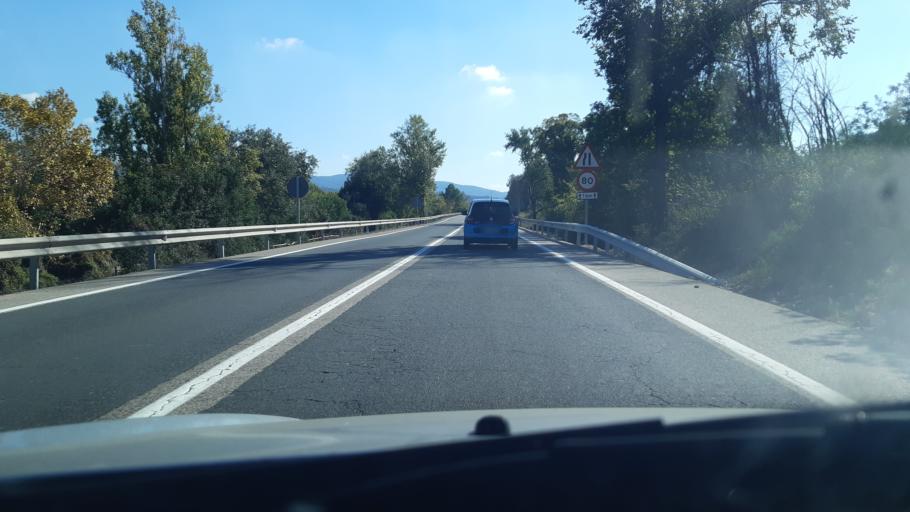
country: ES
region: Catalonia
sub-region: Provincia de Tarragona
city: Tortosa
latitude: 40.8594
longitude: 0.5102
